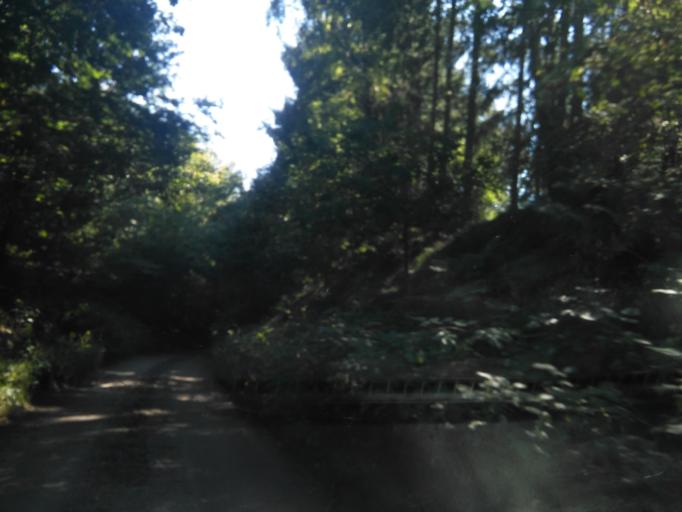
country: DK
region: Central Jutland
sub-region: Syddjurs Kommune
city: Ronde
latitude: 56.2039
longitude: 10.5207
